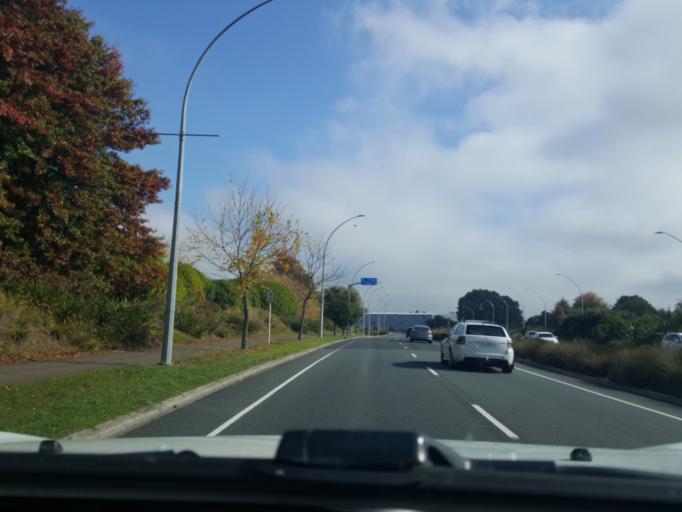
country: NZ
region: Waikato
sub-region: Hamilton City
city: Hamilton
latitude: -37.7471
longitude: 175.2437
